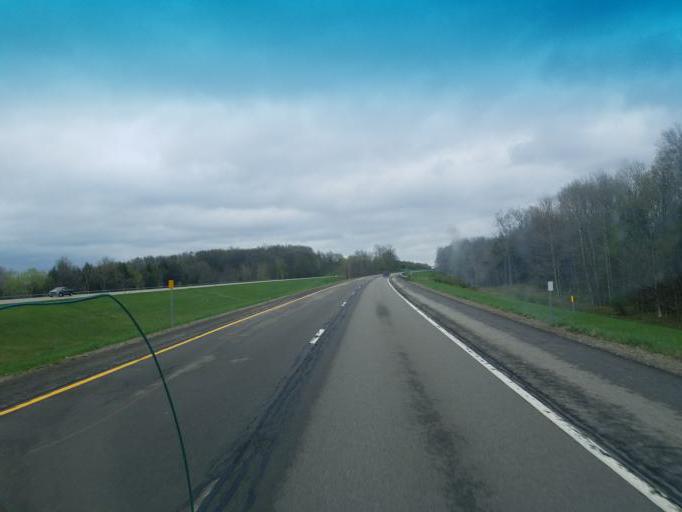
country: US
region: Pennsylvania
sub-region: Erie County
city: North East
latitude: 42.1416
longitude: -79.7185
